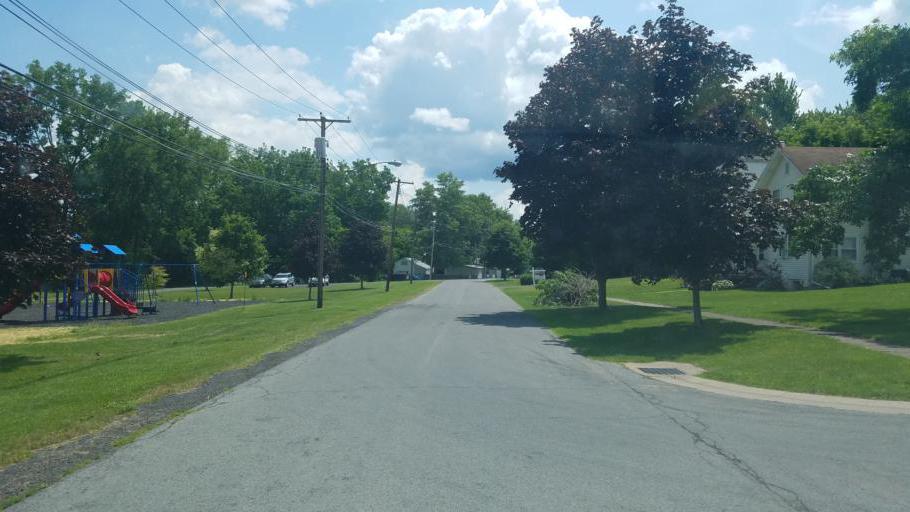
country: US
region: New York
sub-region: Wayne County
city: Clyde
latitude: 43.0799
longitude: -76.8702
